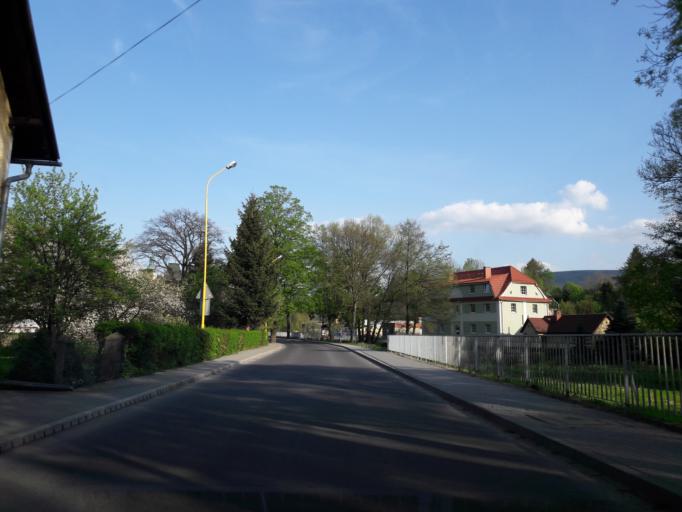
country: PL
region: Lower Silesian Voivodeship
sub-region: Powiat klodzki
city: Szczytna
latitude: 50.4174
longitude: 16.4398
